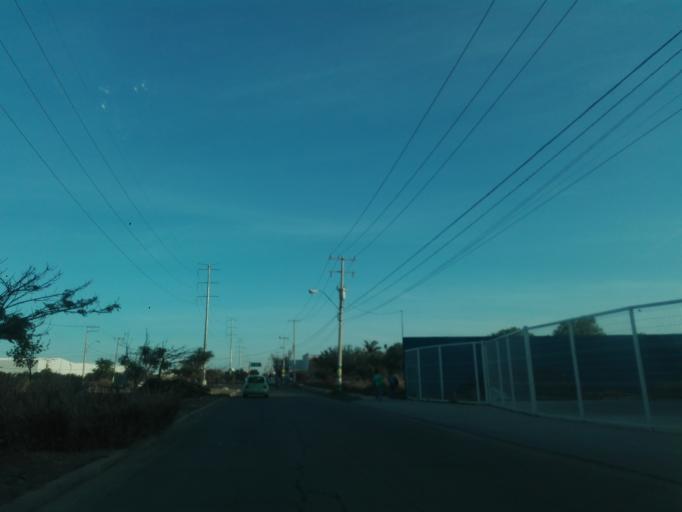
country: MX
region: Guanajuato
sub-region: Leon
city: San Jose de Duran (Los Troncoso)
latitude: 21.0833
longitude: -101.6265
